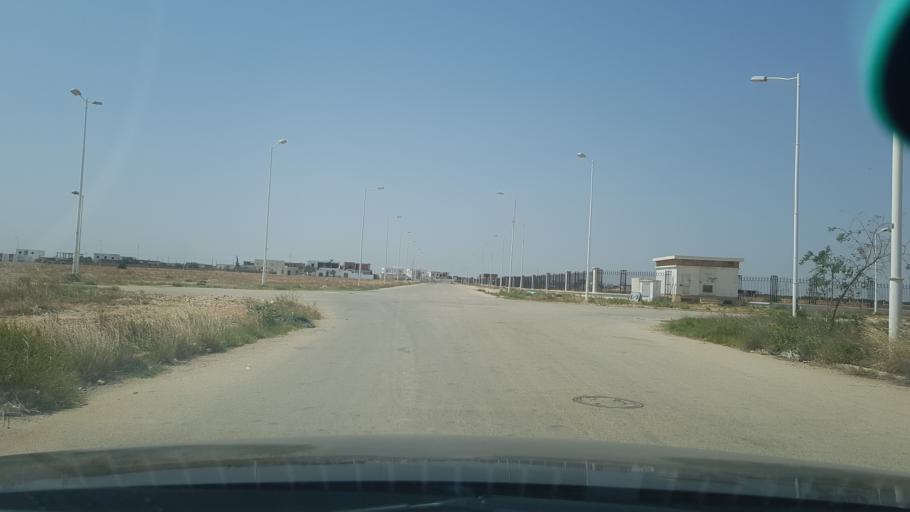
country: TN
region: Safaqis
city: Al Qarmadah
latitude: 34.8330
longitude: 10.7508
